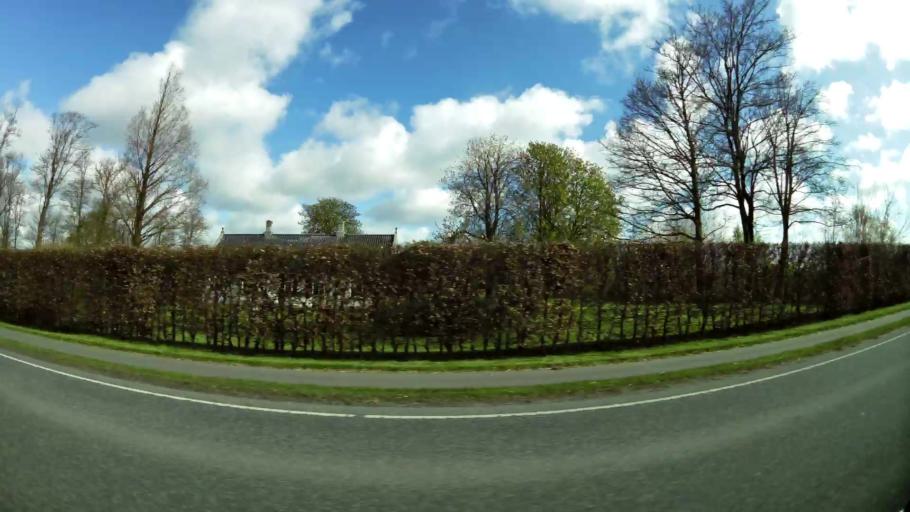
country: DK
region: North Denmark
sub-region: Mariagerfjord Kommune
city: Hobro
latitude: 56.6262
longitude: 9.8352
